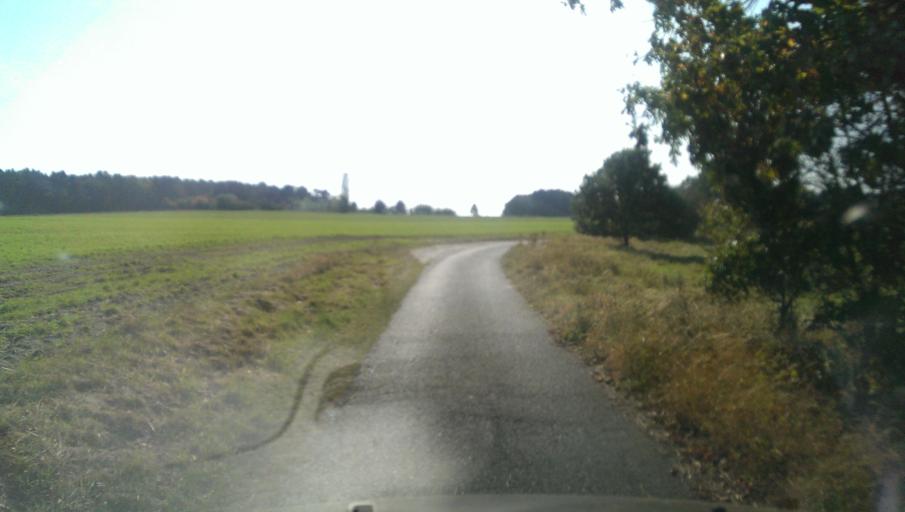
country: DE
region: Brandenburg
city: Sperenberg
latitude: 52.1958
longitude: 13.3350
